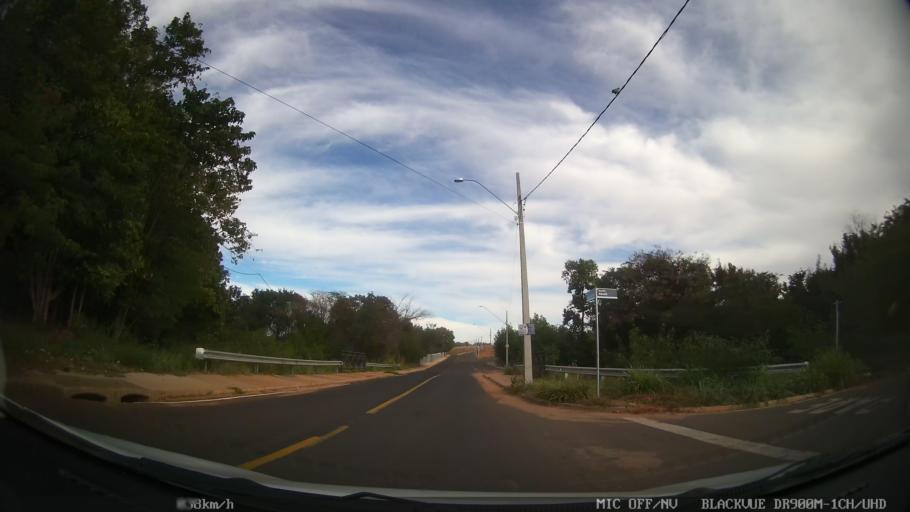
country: BR
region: Sao Paulo
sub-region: Catanduva
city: Catanduva
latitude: -21.1411
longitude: -49.0046
